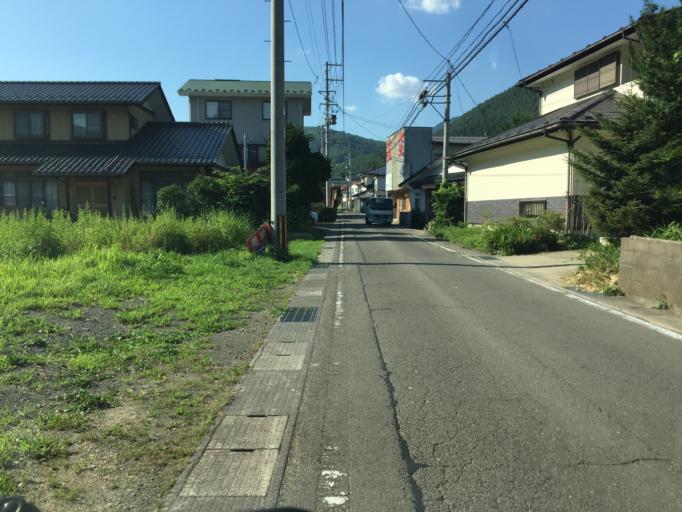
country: JP
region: Fukushima
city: Hobaramachi
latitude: 37.9178
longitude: 140.4251
